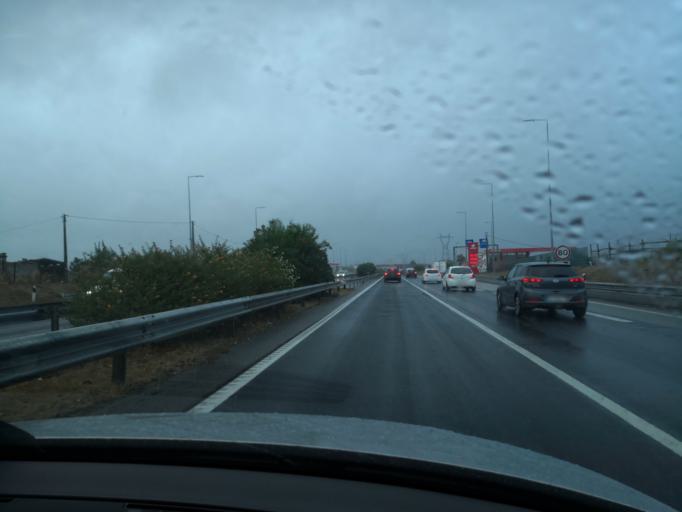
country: PT
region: Setubal
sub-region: Moita
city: Moita
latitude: 38.6621
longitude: -8.9592
